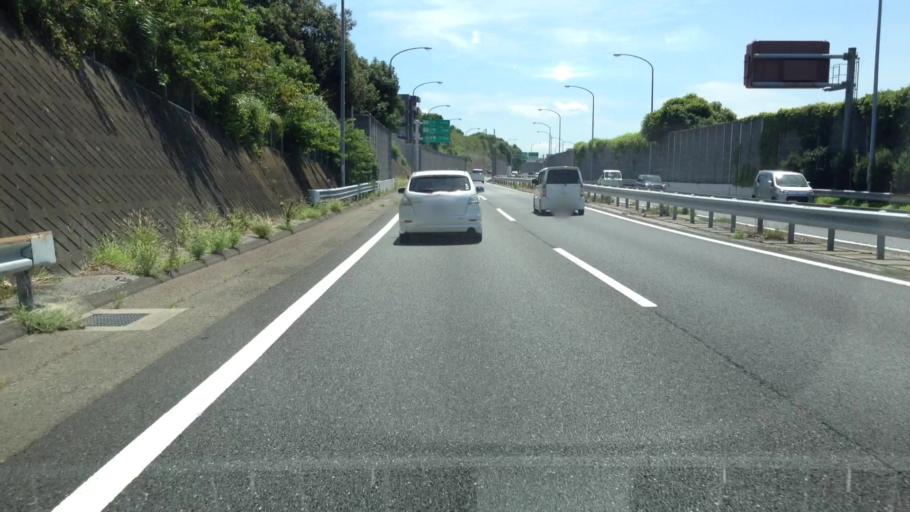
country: JP
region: Kanagawa
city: Yokohama
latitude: 35.4309
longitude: 139.5824
